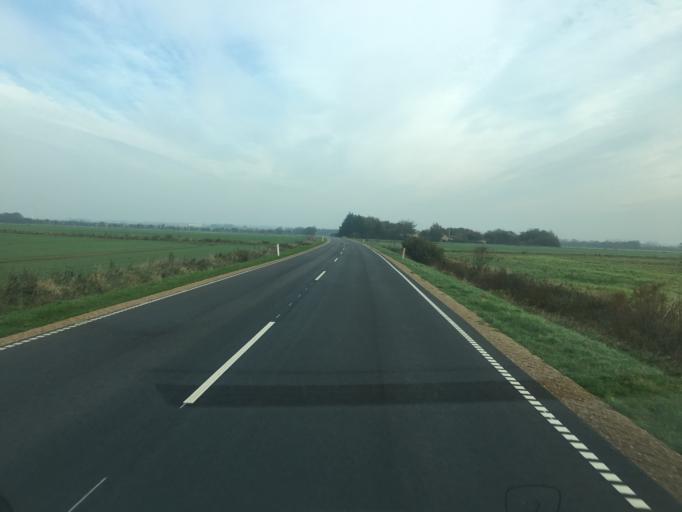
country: DK
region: South Denmark
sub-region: Tonder Kommune
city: Logumkloster
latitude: 55.0995
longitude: 9.0272
